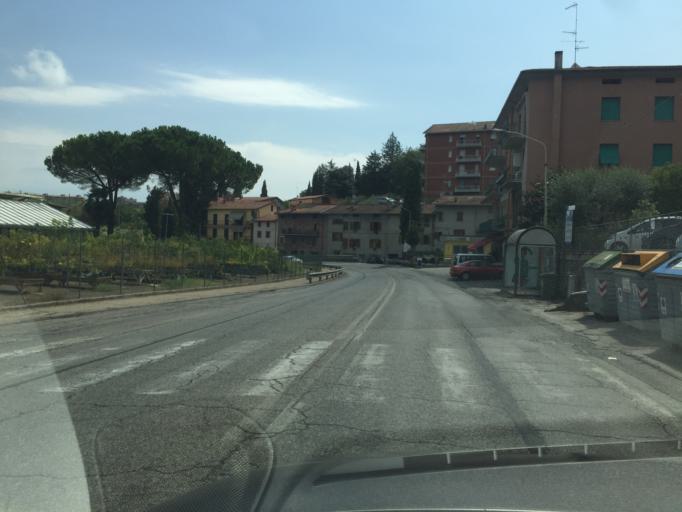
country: IT
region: Umbria
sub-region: Provincia di Perugia
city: Lacugnano
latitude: 43.1052
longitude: 12.3535
